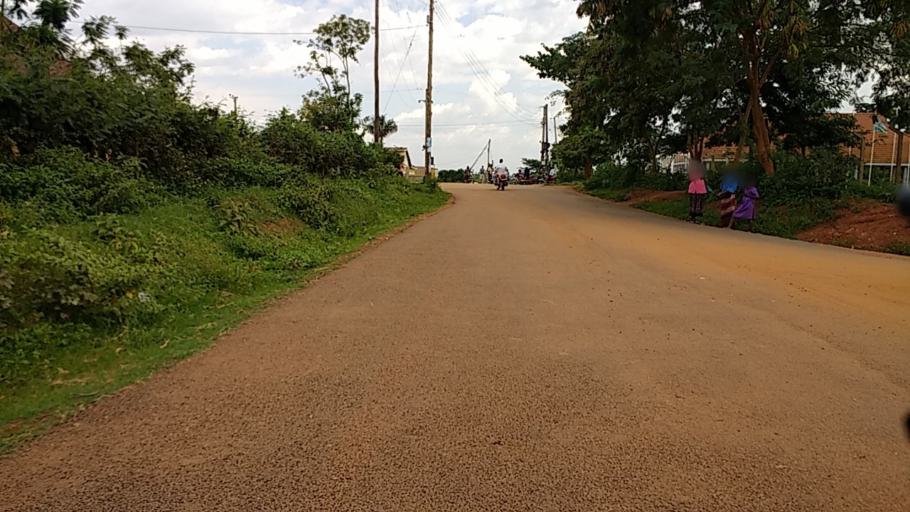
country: UG
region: Eastern Region
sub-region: Mbale District
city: Mbale
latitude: 1.0697
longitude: 34.1695
